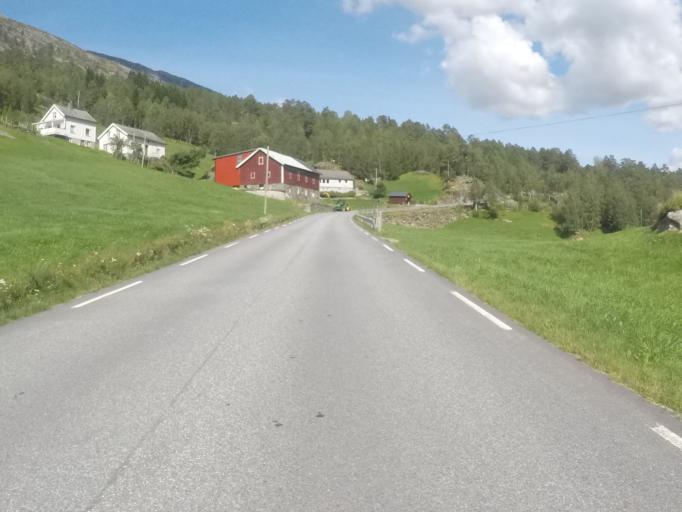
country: NO
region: Sogn og Fjordane
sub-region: Hoyanger
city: Hoyanger
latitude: 61.3210
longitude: 6.2538
